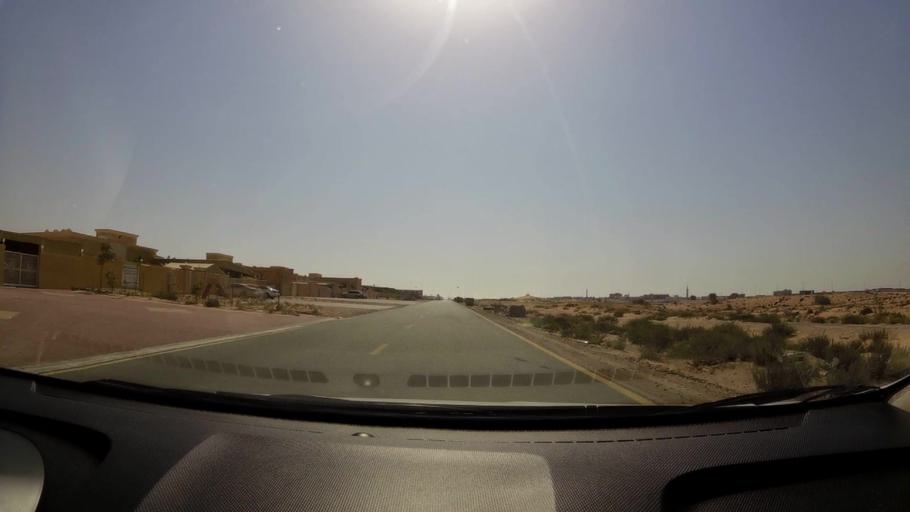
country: AE
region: Umm al Qaywayn
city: Umm al Qaywayn
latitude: 25.4784
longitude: 55.6124
